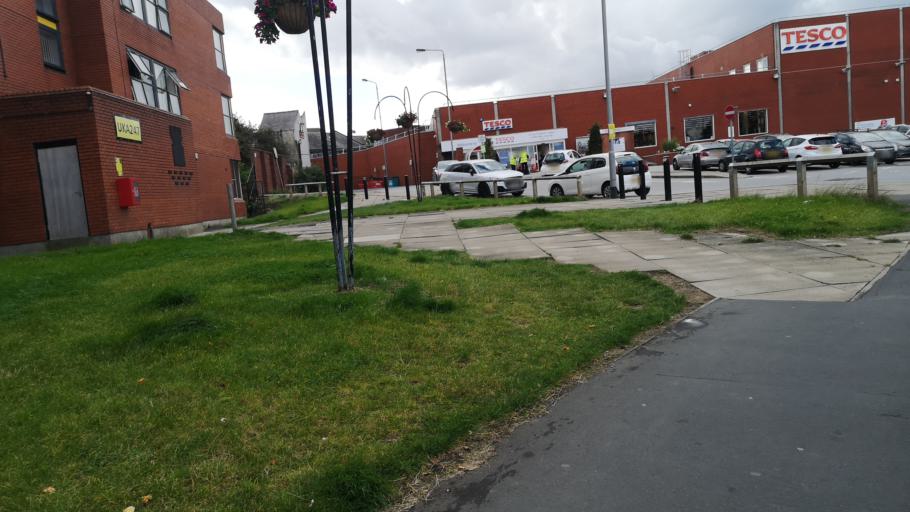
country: GB
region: England
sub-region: City and Borough of Wakefield
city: Pontefract
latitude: 53.6927
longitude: -1.3126
